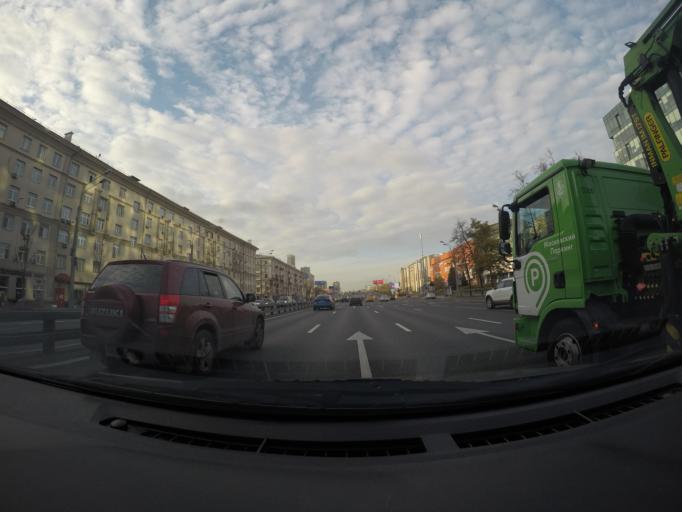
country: RU
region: Moskovskaya
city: Koptevo
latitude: 55.8208
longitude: 37.4965
